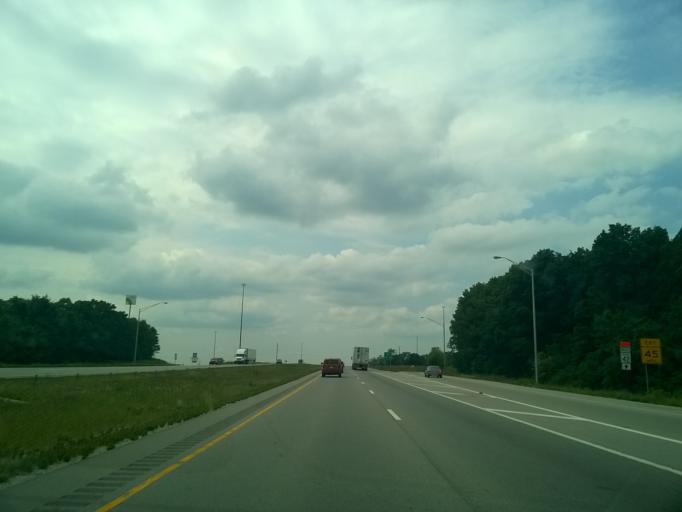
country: US
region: Indiana
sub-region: Putnam County
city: Cloverdale
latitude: 39.5328
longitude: -86.7997
